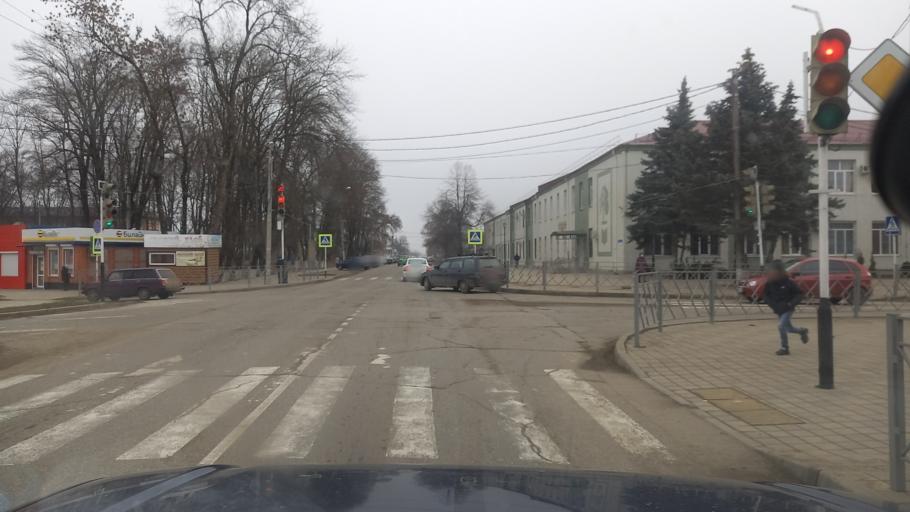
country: RU
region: Krasnodarskiy
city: Apsheronsk
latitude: 44.4627
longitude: 39.7412
